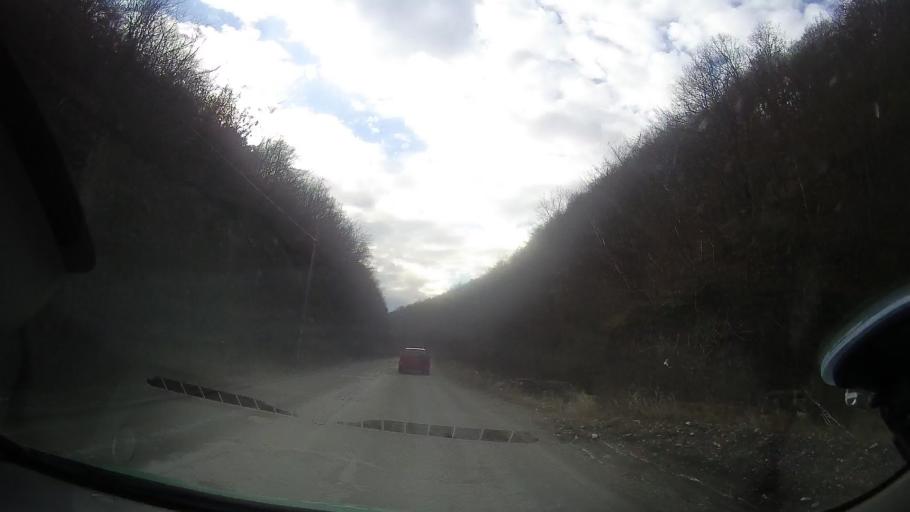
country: RO
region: Cluj
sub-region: Comuna Baisoara
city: Baisoara
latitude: 46.5903
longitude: 23.4586
